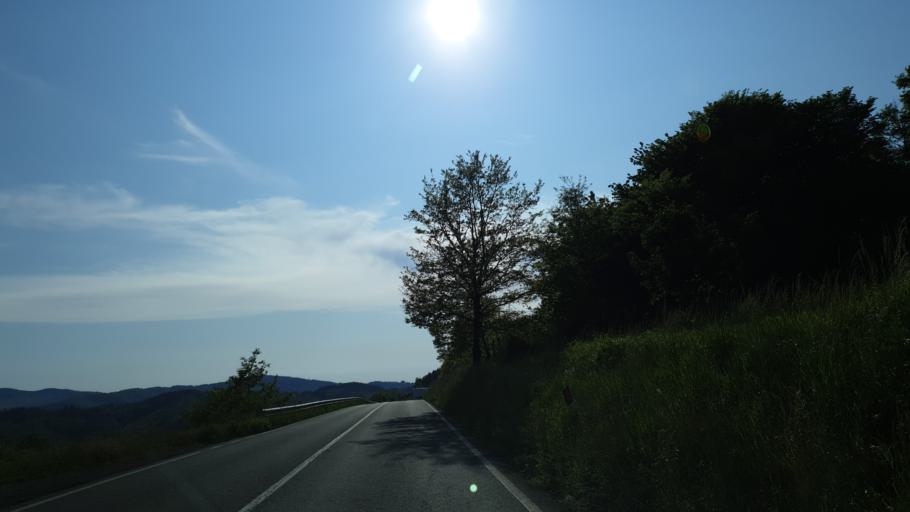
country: IT
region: Tuscany
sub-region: Province of Arezzo
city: Stia
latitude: 43.7815
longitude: 11.6591
